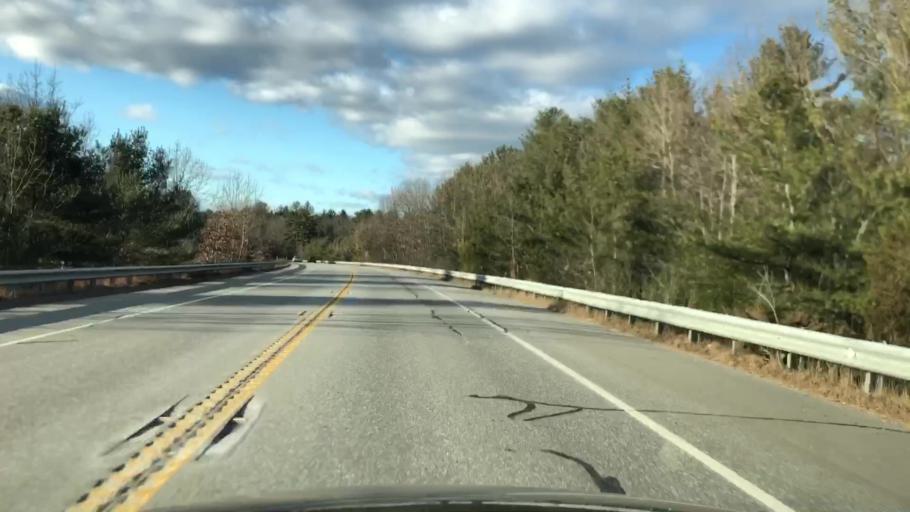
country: US
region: New Hampshire
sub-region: Hillsborough County
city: Milford
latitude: 42.8242
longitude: -71.6615
